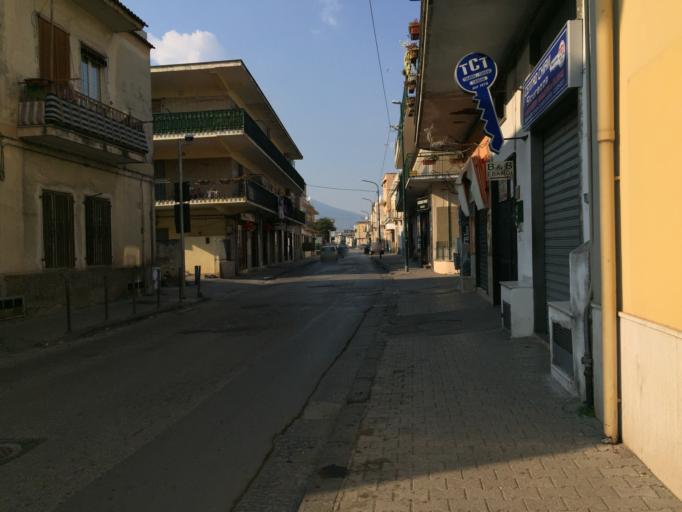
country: IT
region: Campania
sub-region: Provincia di Napoli
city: Pompei
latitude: 40.7520
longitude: 14.5000
